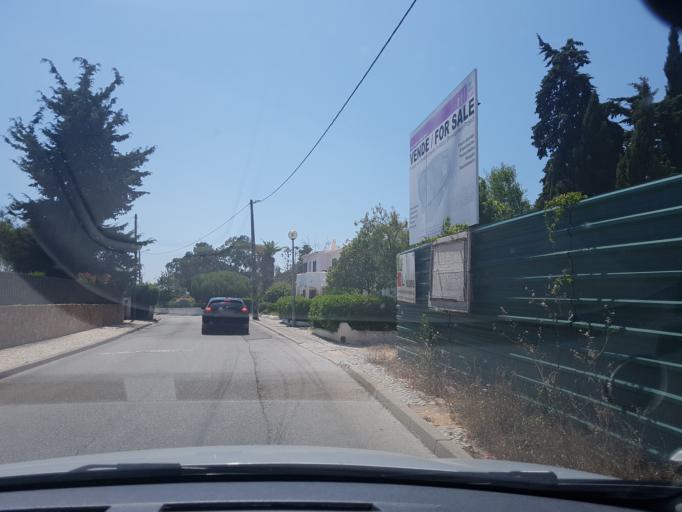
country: PT
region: Faro
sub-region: Lagoa
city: Carvoeiro
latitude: 37.0973
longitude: -8.4601
